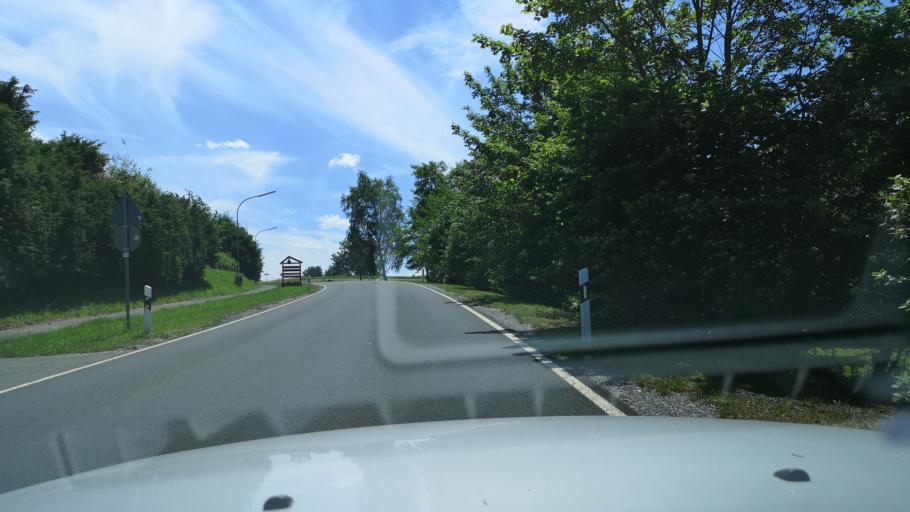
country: DE
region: Bavaria
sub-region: Upper Franconia
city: Teuschnitz
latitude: 50.3968
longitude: 11.3849
